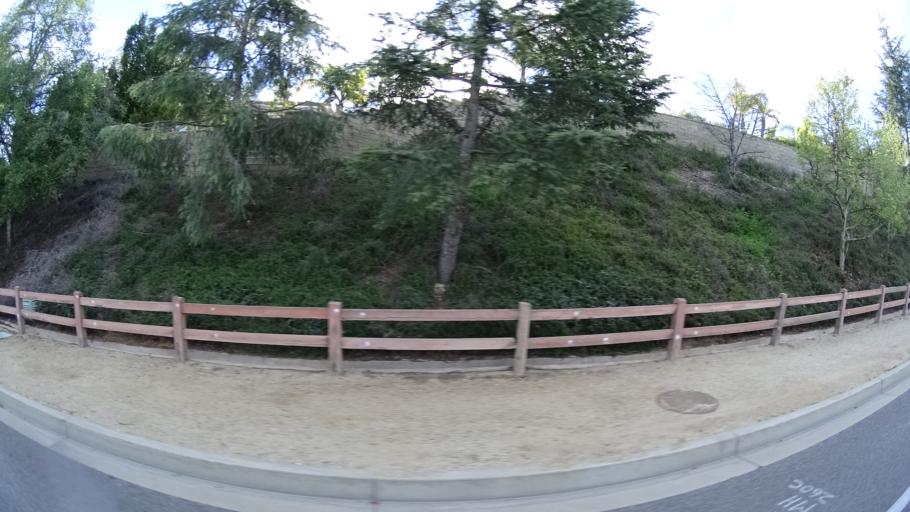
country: US
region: California
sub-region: Ventura County
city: Thousand Oaks
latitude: 34.2062
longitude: -118.8290
